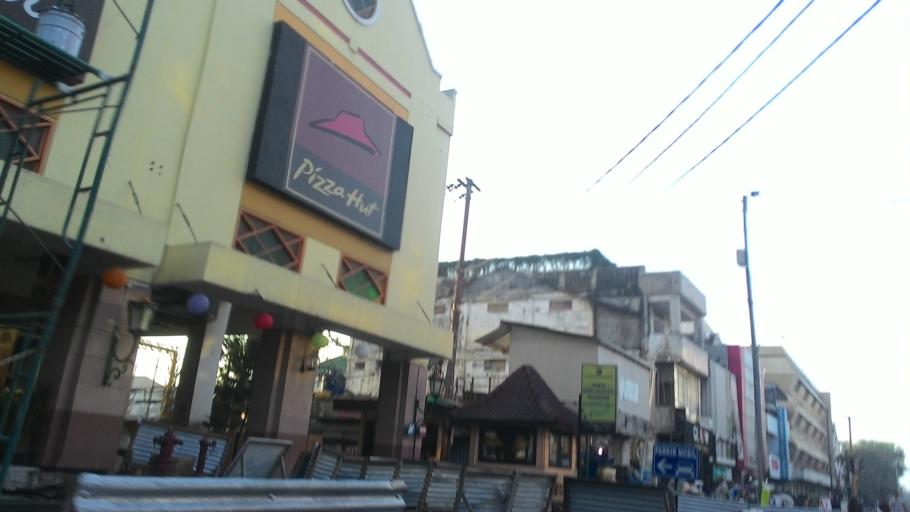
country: ID
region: Daerah Istimewa Yogyakarta
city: Yogyakarta
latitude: -7.7935
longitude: 110.3658
